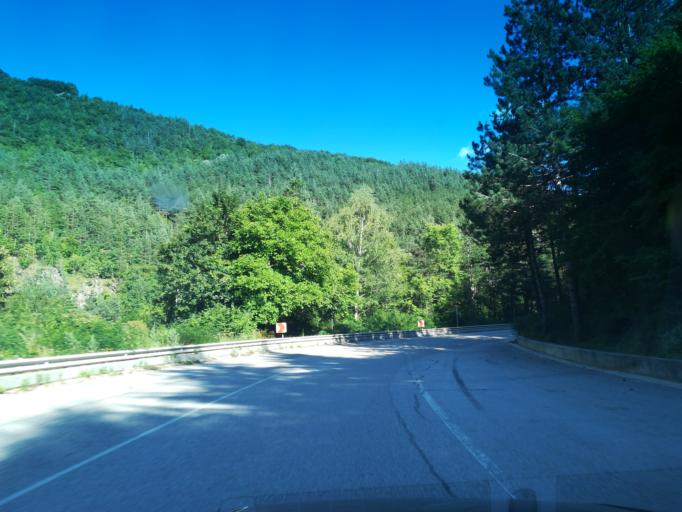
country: BG
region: Smolyan
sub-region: Obshtina Chepelare
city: Chepelare
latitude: 41.8260
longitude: 24.6916
